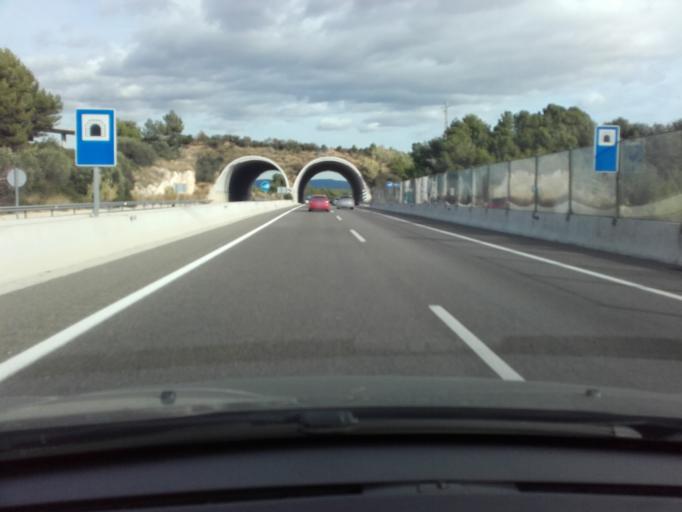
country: ES
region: Catalonia
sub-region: Provincia de Tarragona
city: el Catllar
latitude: 41.1471
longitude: 1.2920
